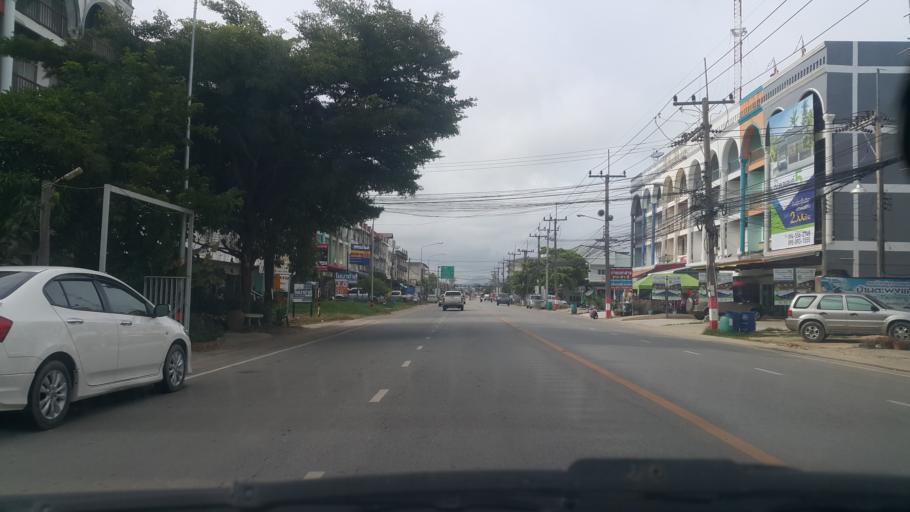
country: TH
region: Rayong
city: Rayong
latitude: 12.6438
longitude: 101.3450
